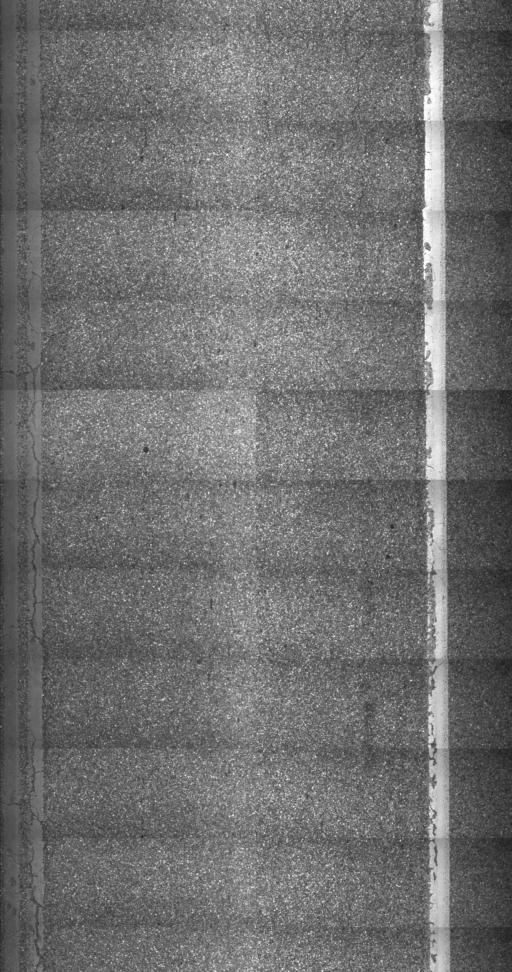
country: US
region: Vermont
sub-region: Bennington County
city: Manchester Center
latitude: 43.2550
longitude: -73.0989
